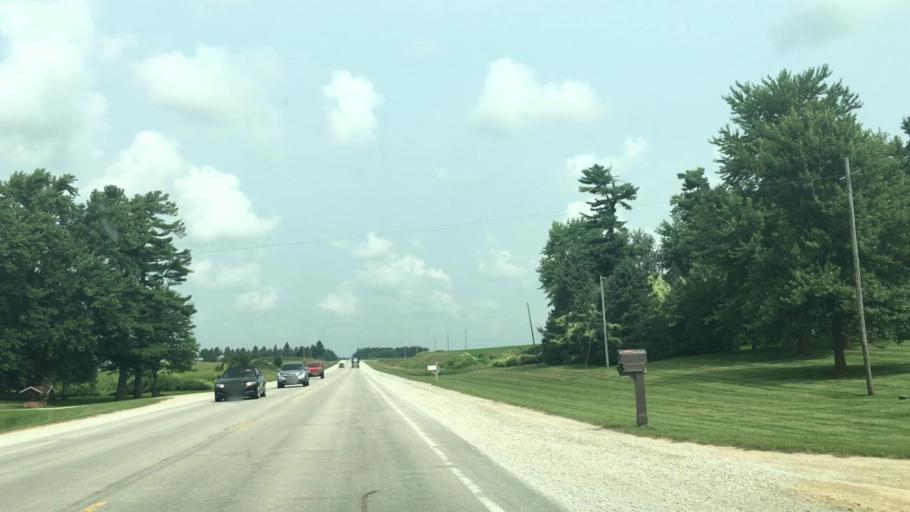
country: US
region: Minnesota
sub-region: Fillmore County
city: Harmony
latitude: 43.4807
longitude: -91.8703
